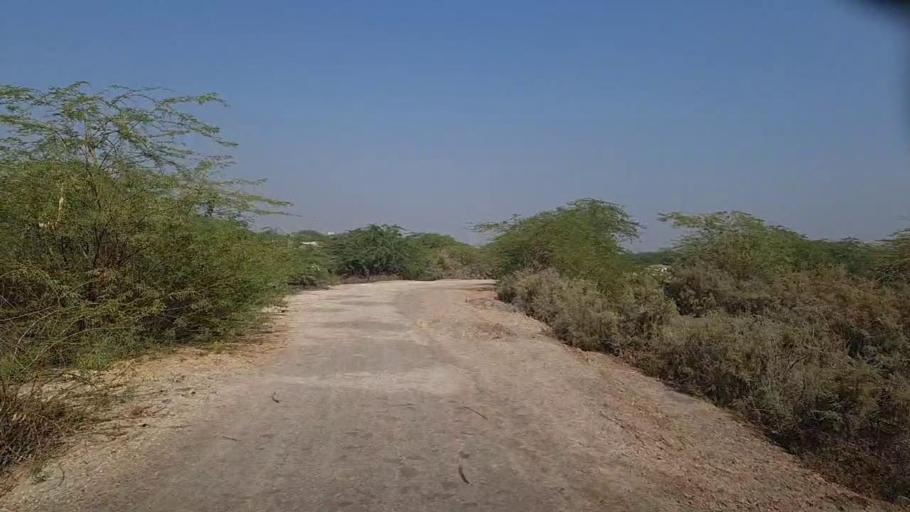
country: PK
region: Sindh
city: Bozdar
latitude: 27.2518
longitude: 68.5975
